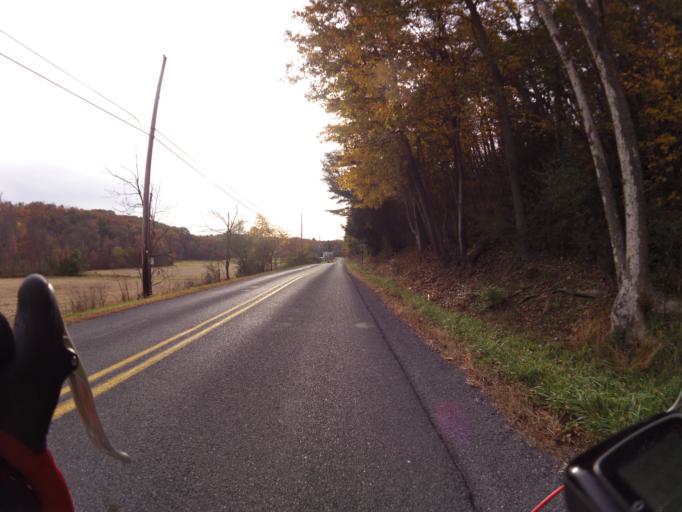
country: US
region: Pennsylvania
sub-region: Union County
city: New Columbia
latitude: 41.0318
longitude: -76.9428
